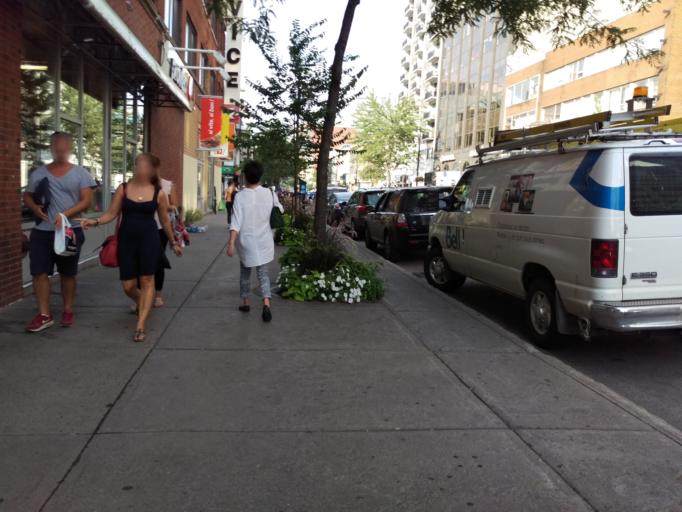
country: CA
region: Quebec
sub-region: Montreal
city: Montreal
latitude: 45.4920
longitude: -73.5814
